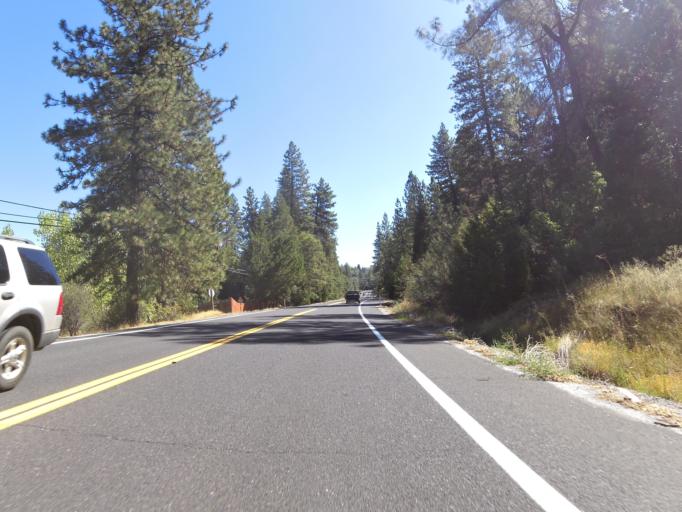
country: US
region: California
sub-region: Calaveras County
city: Forest Meadows
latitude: 38.1770
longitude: -120.3900
